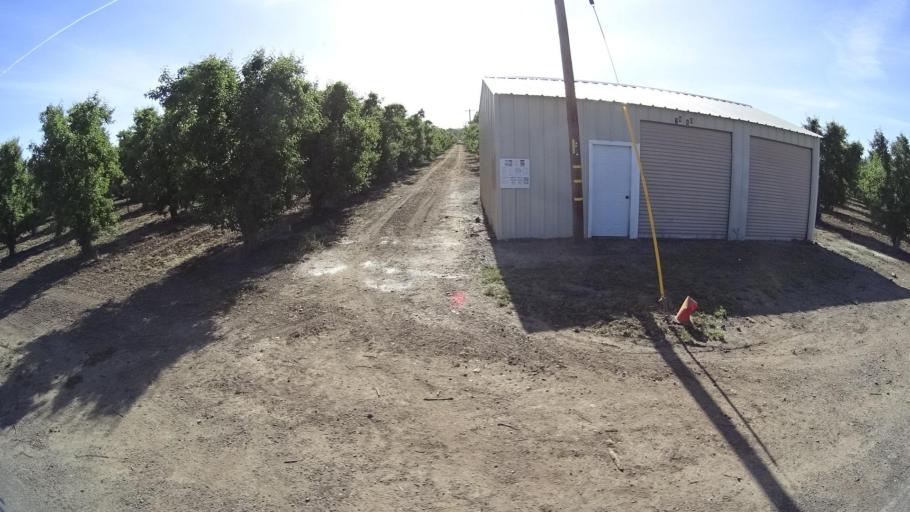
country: US
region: California
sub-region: Lake County
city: Kelseyville
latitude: 39.0130
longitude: -122.8476
